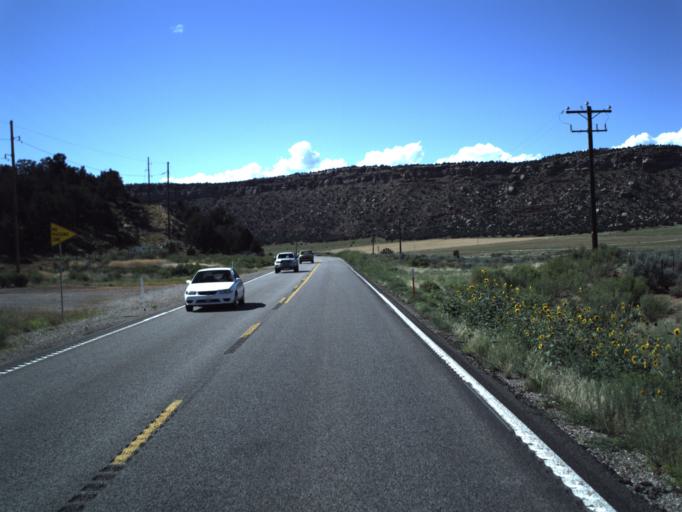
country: US
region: Utah
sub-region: Washington County
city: LaVerkin
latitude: 37.1151
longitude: -113.1544
